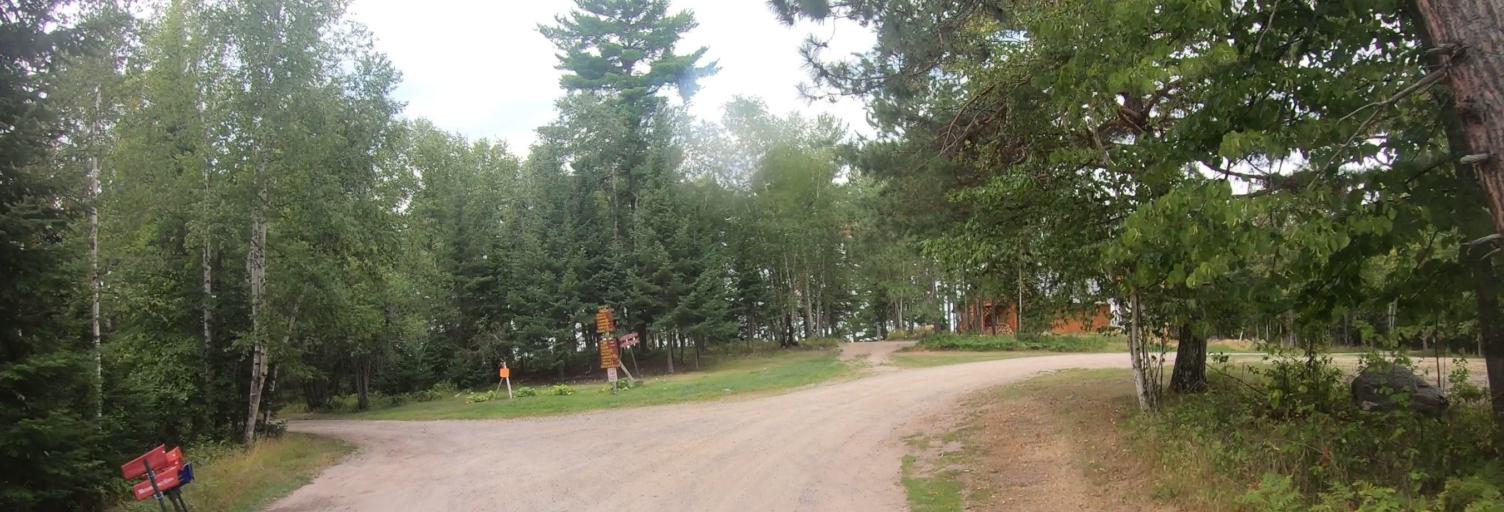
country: US
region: Minnesota
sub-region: Saint Louis County
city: Mountain Iron
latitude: 47.9427
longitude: -92.6285
